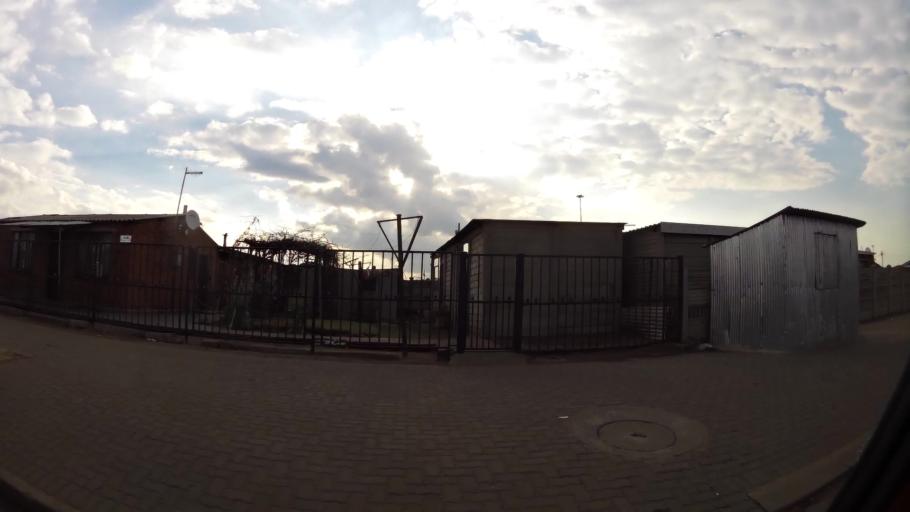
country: ZA
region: Gauteng
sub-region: Sedibeng District Municipality
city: Vanderbijlpark
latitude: -26.6954
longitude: 27.8771
